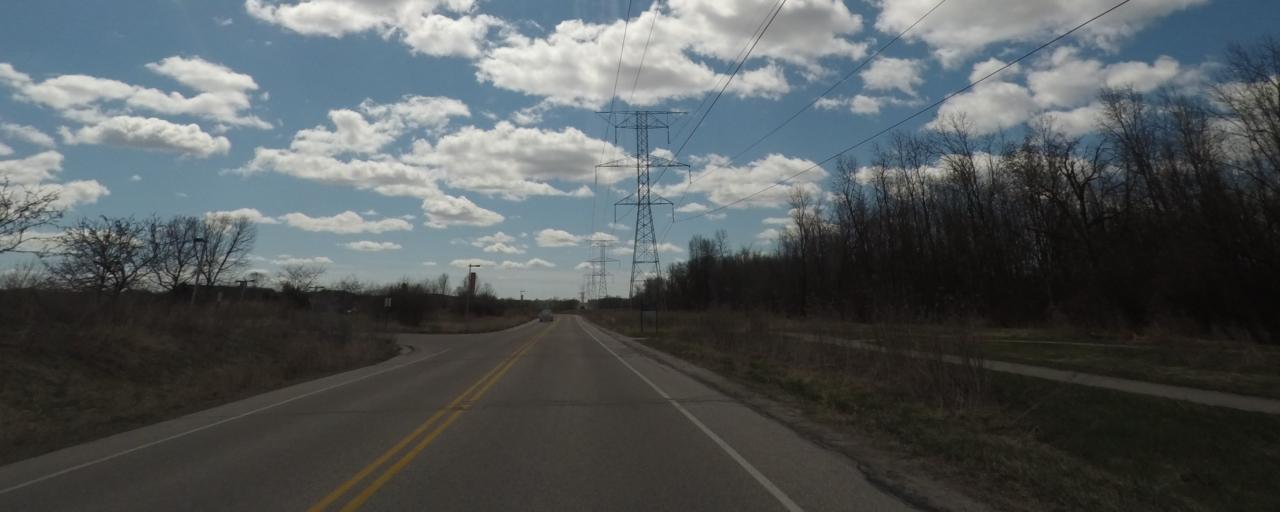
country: US
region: Wisconsin
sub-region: Waukesha County
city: Brookfield
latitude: 43.0783
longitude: -88.1607
